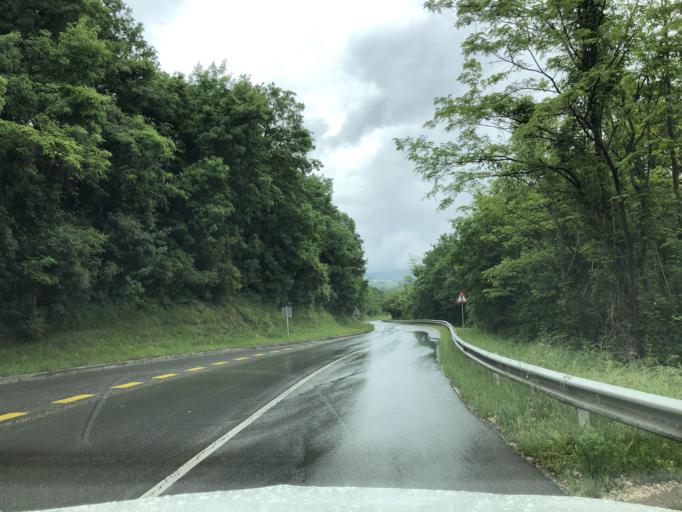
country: SI
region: Koper-Capodistria
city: Prade
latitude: 45.5035
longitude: 13.7726
